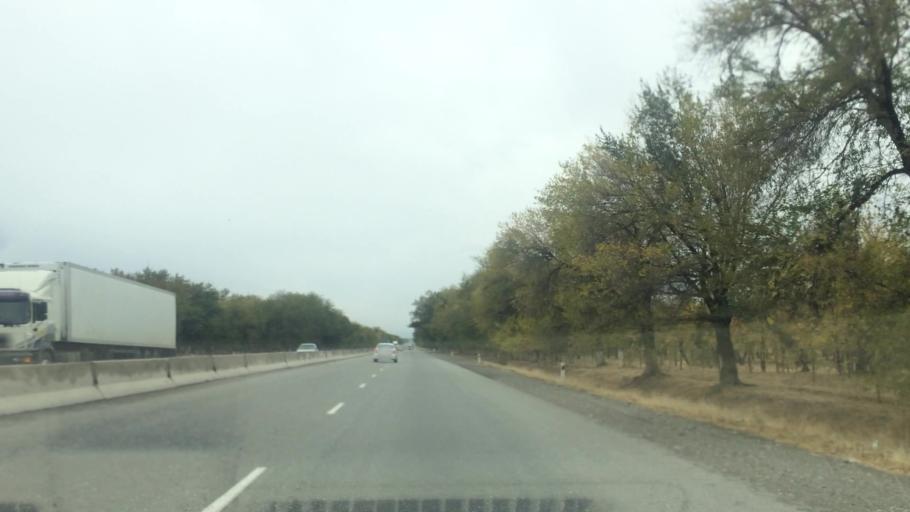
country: UZ
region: Samarqand
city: Bulung'ur
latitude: 39.8006
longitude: 67.3430
